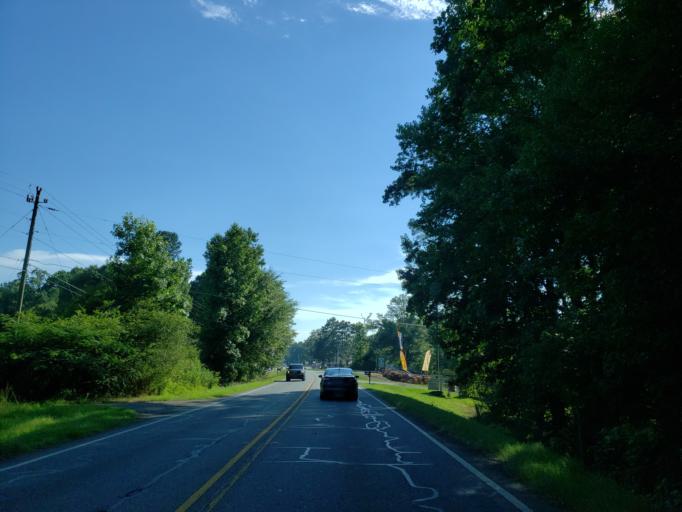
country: US
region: Georgia
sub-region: Fulton County
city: Milton
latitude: 34.2357
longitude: -84.2629
